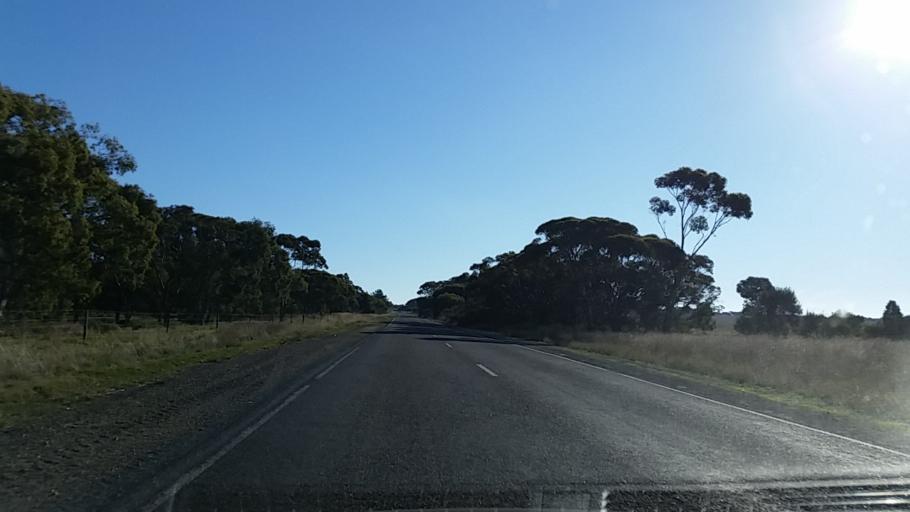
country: AU
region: South Australia
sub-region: Mount Barker
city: Callington
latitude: -35.1136
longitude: 139.0908
